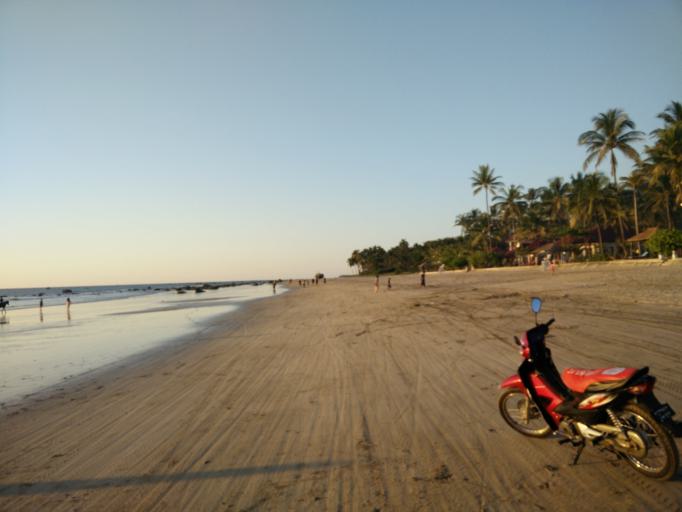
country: MM
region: Ayeyarwady
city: Pathein
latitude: 16.8306
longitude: 94.3947
